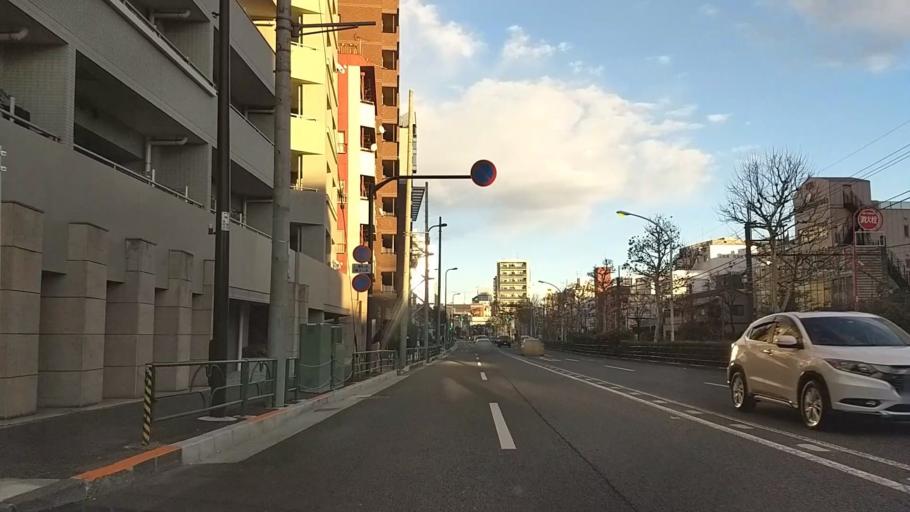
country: JP
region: Tokyo
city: Tokyo
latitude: 35.7165
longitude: 139.7003
